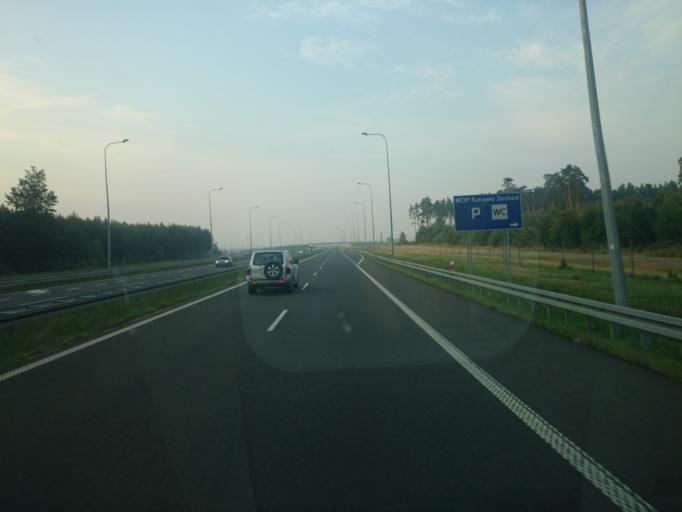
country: PL
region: West Pomeranian Voivodeship
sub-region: Powiat pyrzycki
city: Bielice
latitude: 53.1560
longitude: 14.7100
